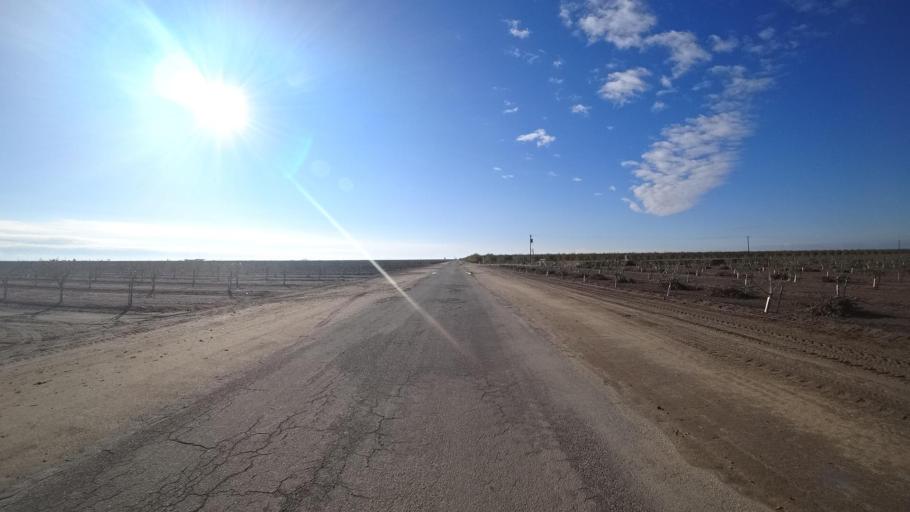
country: US
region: California
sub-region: Kern County
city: McFarland
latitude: 35.7120
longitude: -119.2941
